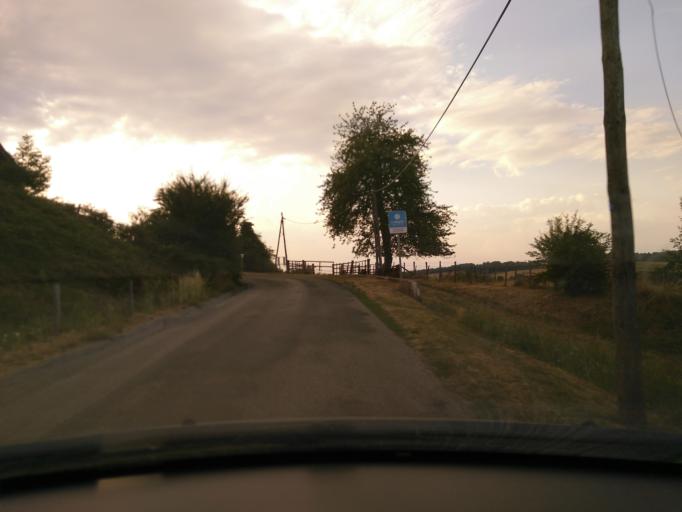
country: FR
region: Rhone-Alpes
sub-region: Departement de l'Isere
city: Beaurepaire
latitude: 45.4004
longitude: 5.1211
